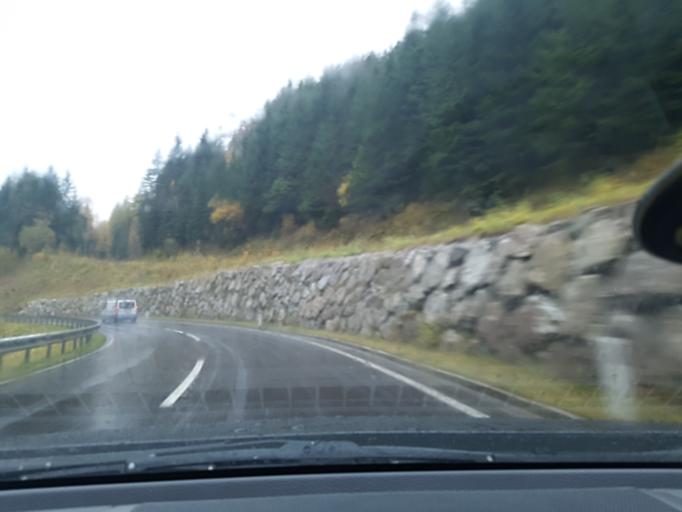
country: AT
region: Styria
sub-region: Politischer Bezirk Liezen
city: Trieben
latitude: 47.4649
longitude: 14.4864
